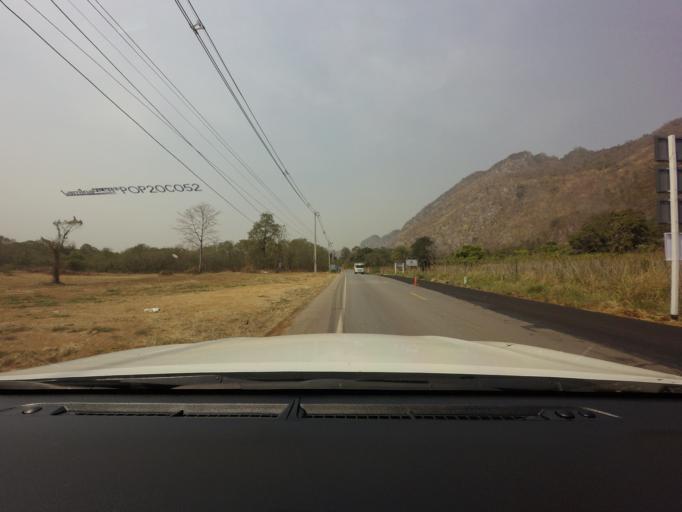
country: TH
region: Sara Buri
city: Muak Lek
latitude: 14.5814
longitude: 101.2584
